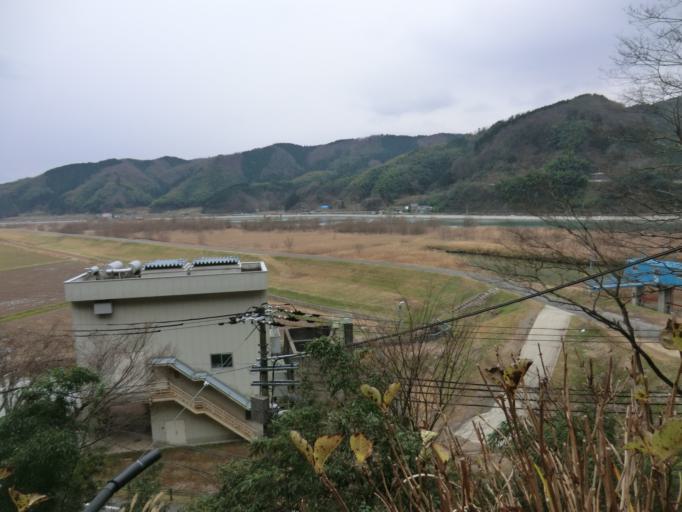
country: JP
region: Hyogo
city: Toyooka
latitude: 35.5875
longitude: 134.8047
